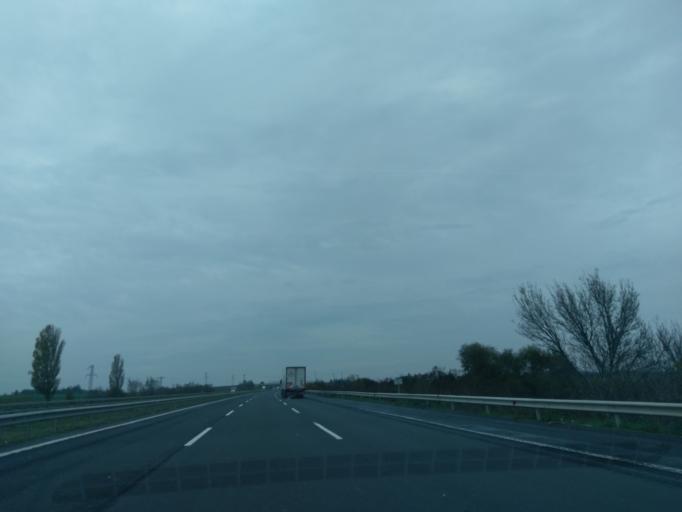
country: TR
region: Istanbul
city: Canta
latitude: 41.1355
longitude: 28.1534
